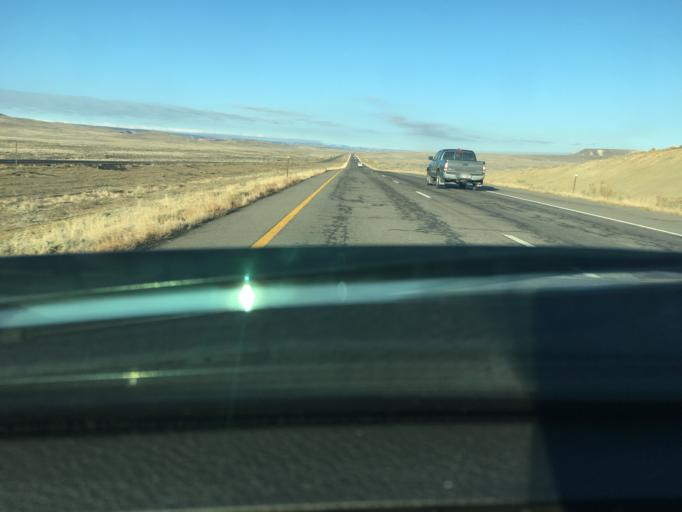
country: US
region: Colorado
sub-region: Delta County
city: Delta
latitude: 38.7612
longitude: -108.1963
